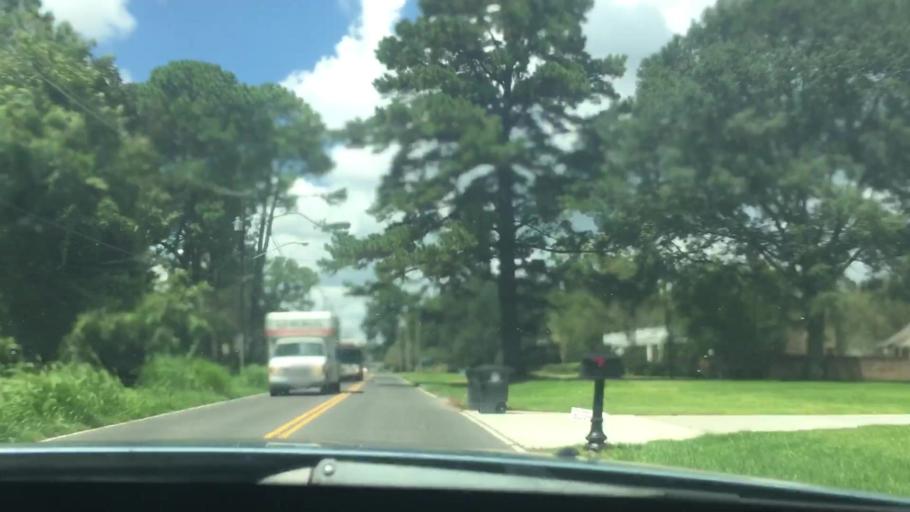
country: US
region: Louisiana
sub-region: East Baton Rouge Parish
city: Gardere
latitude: 30.3738
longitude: -91.1325
